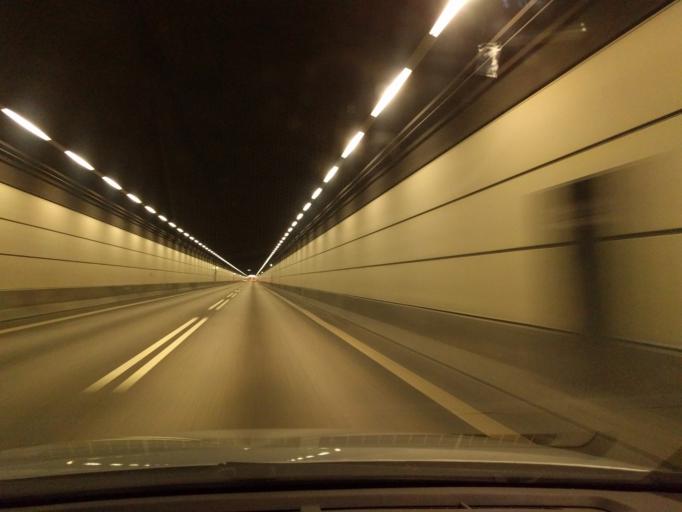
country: DK
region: Capital Region
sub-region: Dragor Kommune
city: Dragor
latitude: 55.6166
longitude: 12.7130
